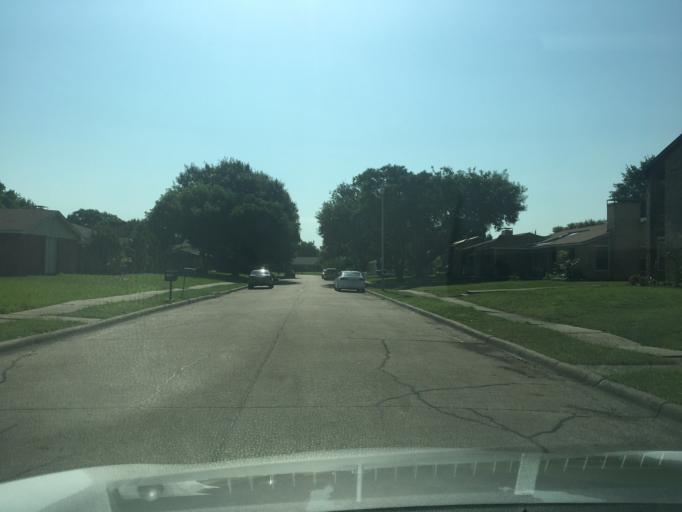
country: US
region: Texas
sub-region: Dallas County
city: Richardson
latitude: 32.9287
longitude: -96.6899
